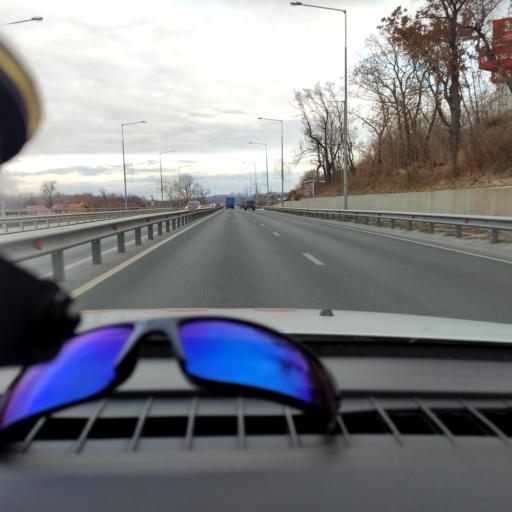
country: RU
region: Samara
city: Volzhskiy
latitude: 53.3947
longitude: 50.1538
